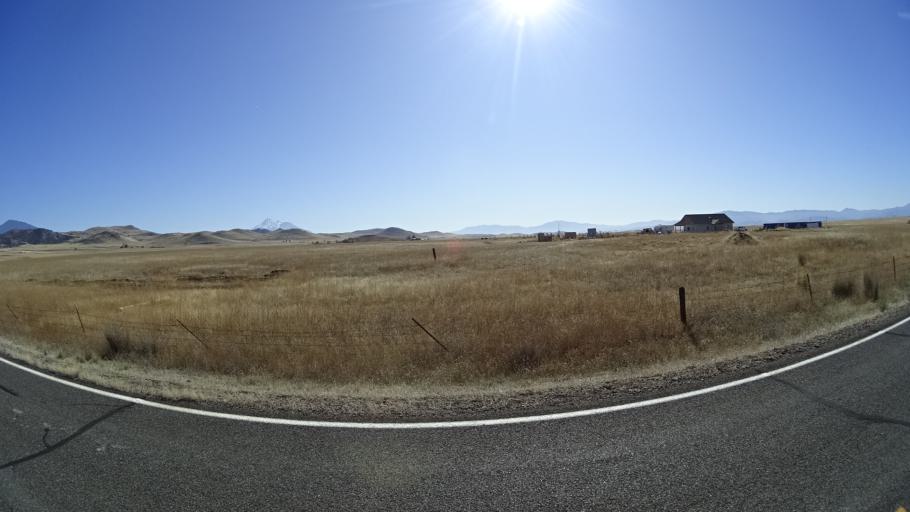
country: US
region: California
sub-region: Siskiyou County
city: Montague
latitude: 41.8082
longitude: -122.4358
